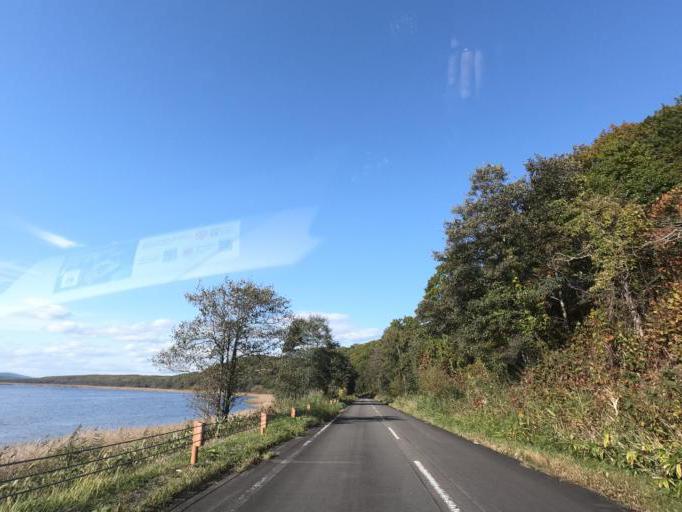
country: JP
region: Hokkaido
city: Obihiro
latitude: 42.6128
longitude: 143.5443
